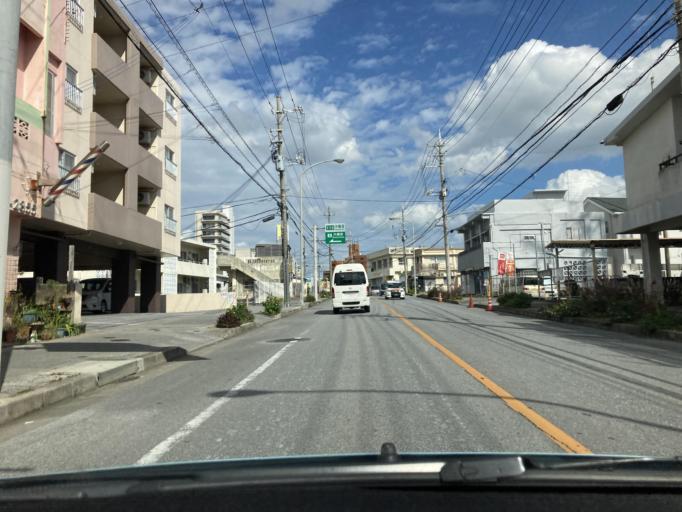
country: JP
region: Okinawa
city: Okinawa
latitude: 26.3212
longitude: 127.7876
